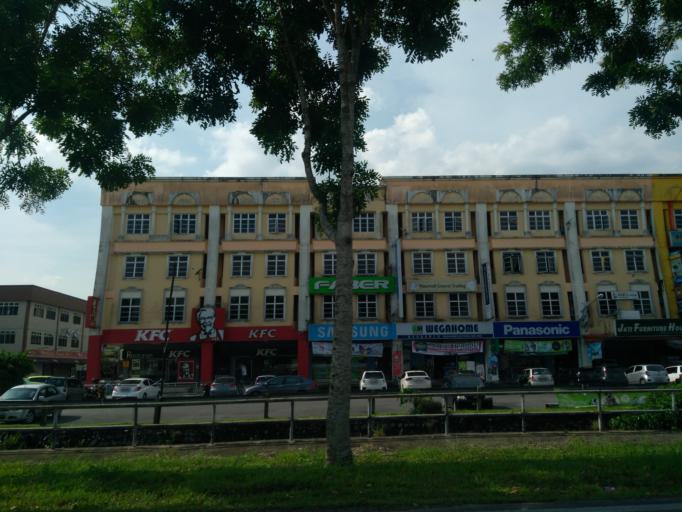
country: MY
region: Sarawak
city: Kuching
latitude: 1.5735
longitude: 110.2946
